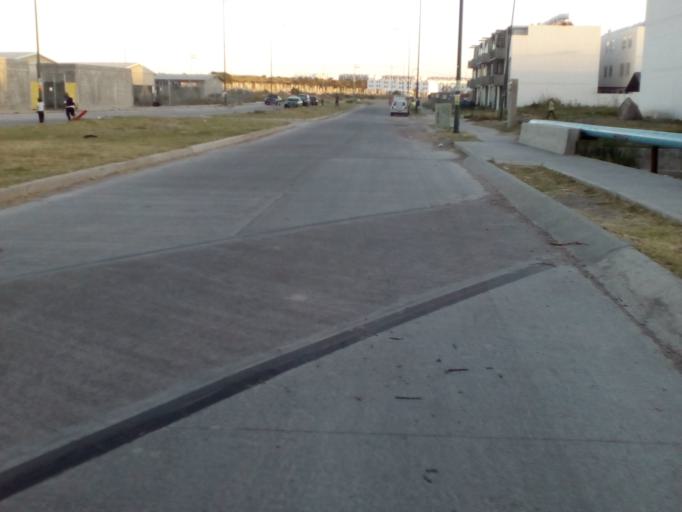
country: MX
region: Guanajuato
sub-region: Leon
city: Fraccionamiento Paseo de las Torres
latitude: 21.1836
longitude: -101.7669
